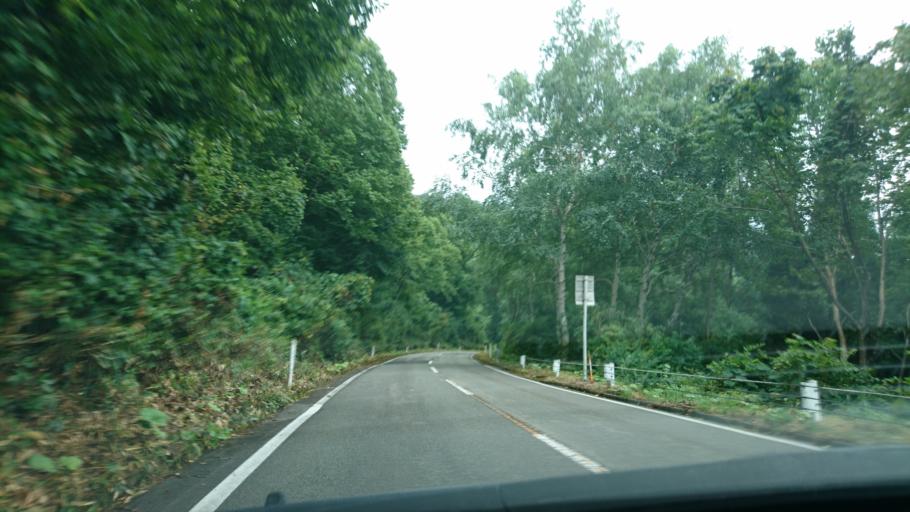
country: JP
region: Akita
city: Yuzawa
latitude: 38.9738
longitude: 140.7228
